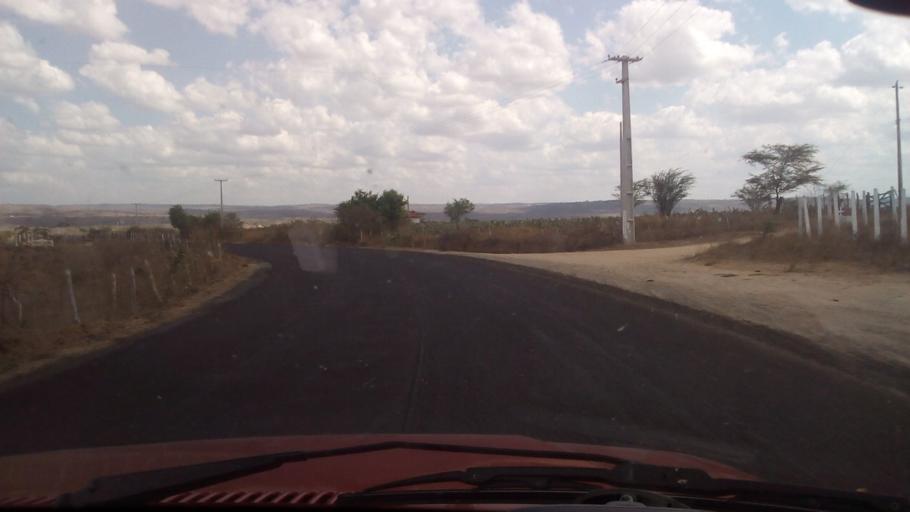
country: BR
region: Paraiba
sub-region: Cacimba De Dentro
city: Cacimba de Dentro
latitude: -6.6660
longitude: -35.7585
